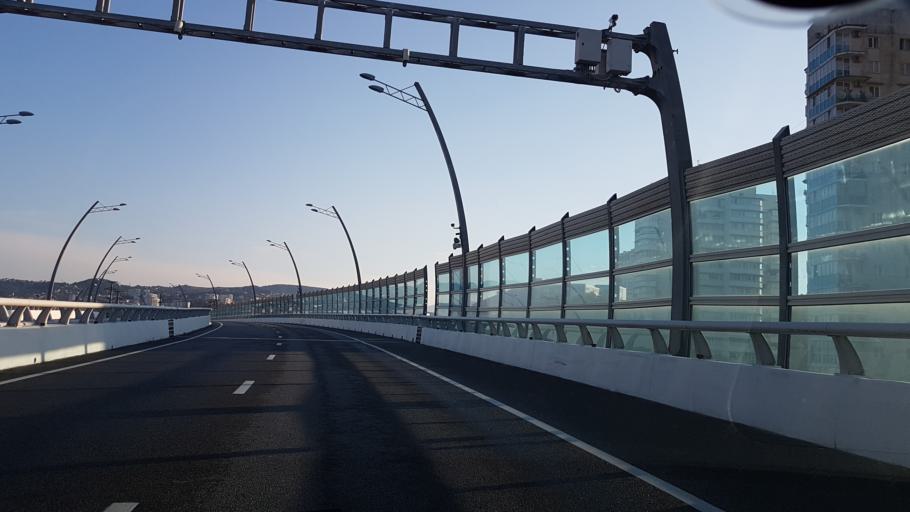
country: RU
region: Krasnodarskiy
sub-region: Sochi City
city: Sochi
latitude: 43.5952
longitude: 39.7317
